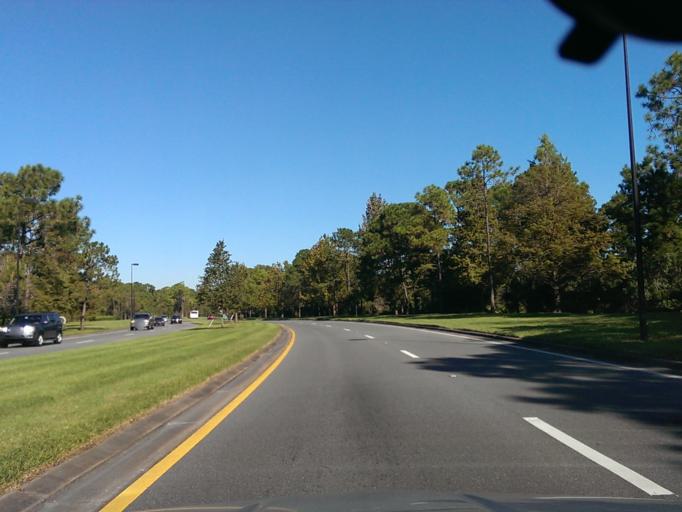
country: US
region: Florida
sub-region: Osceola County
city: Celebration
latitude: 28.3867
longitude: -81.5399
